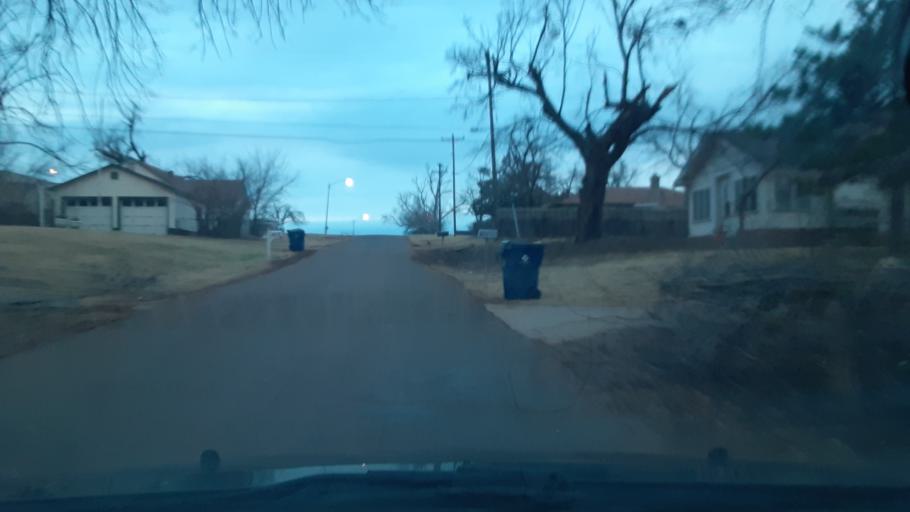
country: US
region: Oklahoma
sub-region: Logan County
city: Guthrie
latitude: 35.8790
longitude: -97.4116
